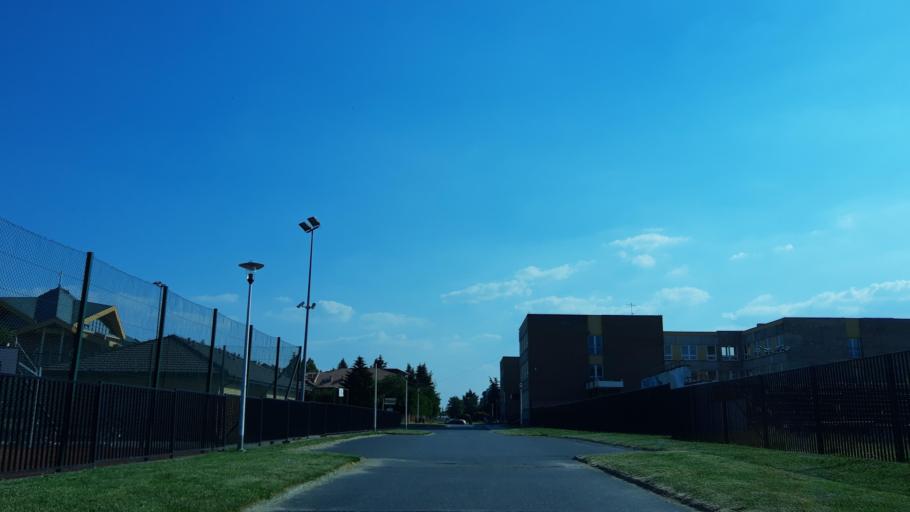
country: PL
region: Lodz Voivodeship
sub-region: Powiat sieradzki
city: Sieradz
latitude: 51.5918
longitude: 18.7184
